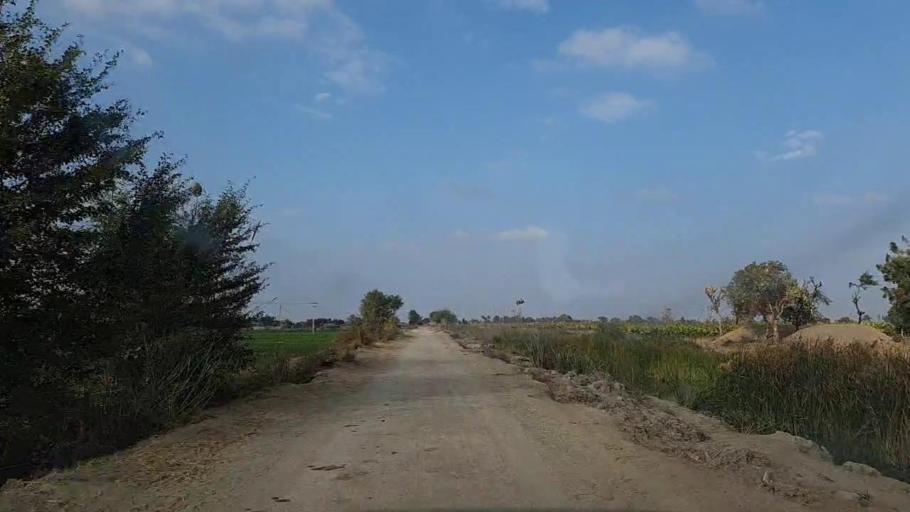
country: PK
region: Sindh
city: Sanghar
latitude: 26.2354
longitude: 68.9729
